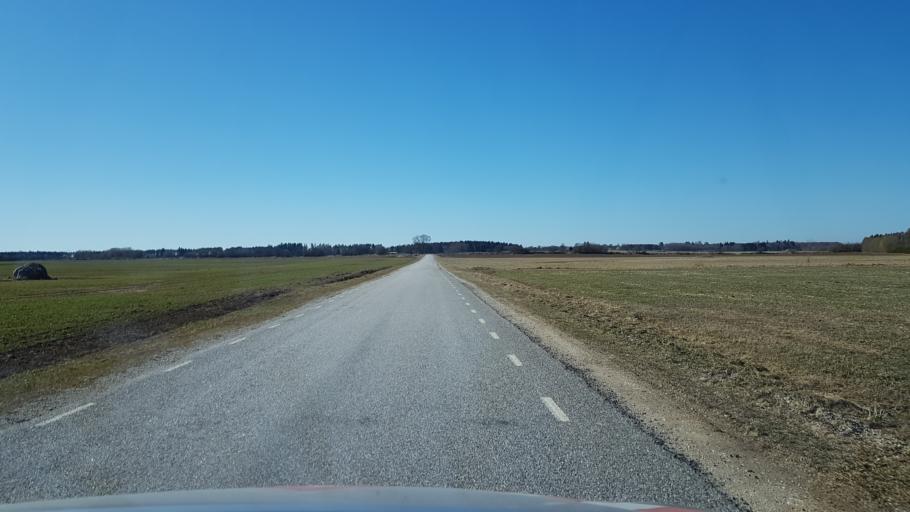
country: EE
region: Laeaene-Virumaa
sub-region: Viru-Nigula vald
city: Kunda
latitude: 59.3982
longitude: 26.5561
